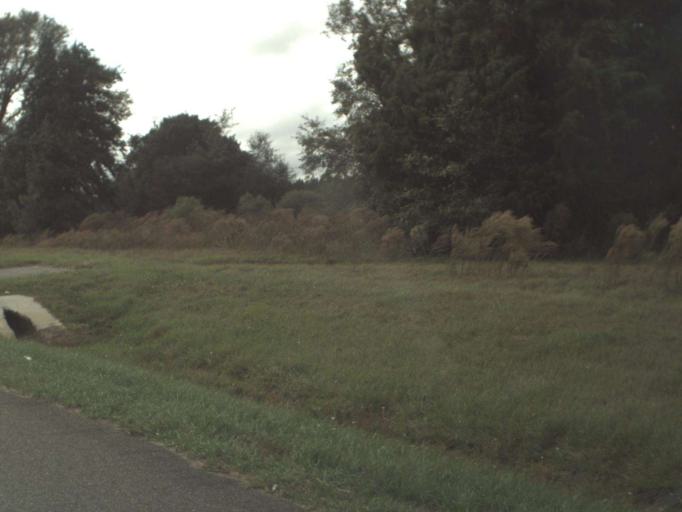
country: US
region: Florida
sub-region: Santa Rosa County
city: Point Baker
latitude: 30.7692
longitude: -87.0929
